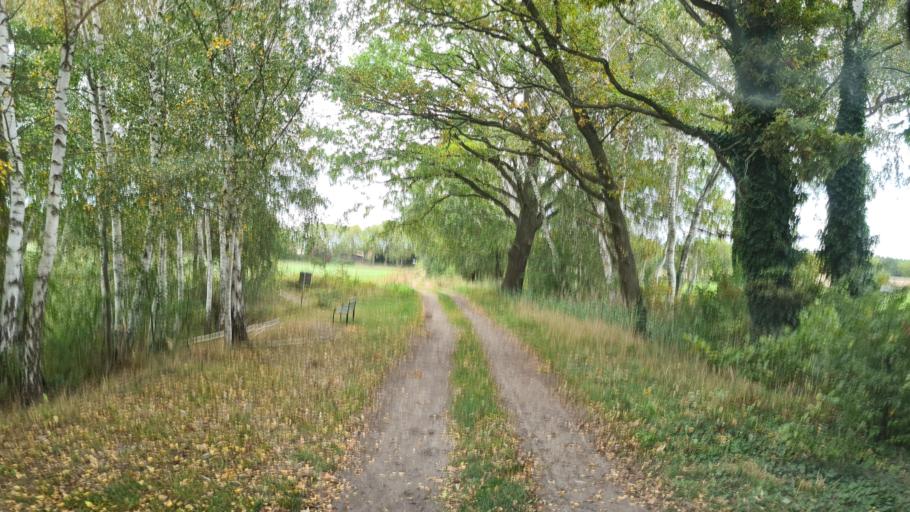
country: DE
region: Brandenburg
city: Zossen
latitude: 52.2458
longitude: 13.4848
